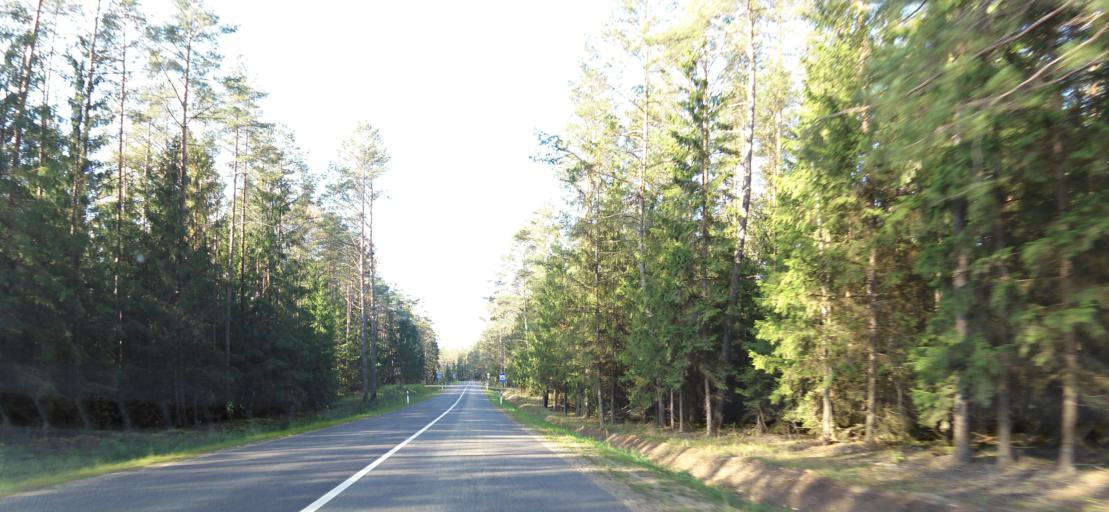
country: LT
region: Vilnius County
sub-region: Trakai
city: Rudiskes
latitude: 54.5097
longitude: 24.8909
